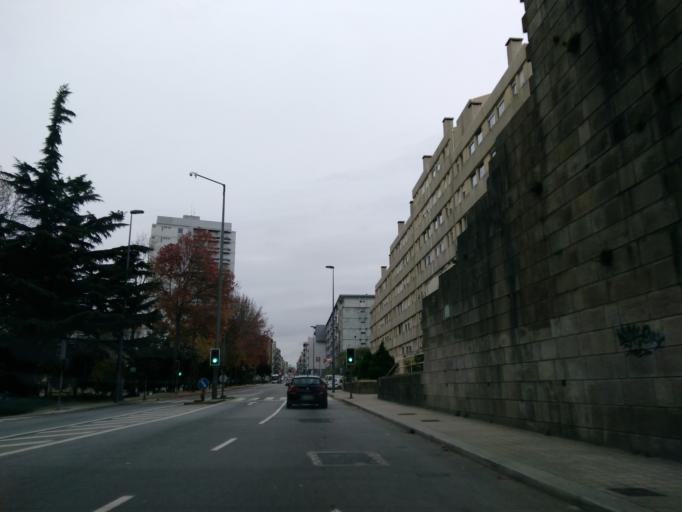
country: PT
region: Porto
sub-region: Porto
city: Porto
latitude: 41.1521
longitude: -8.5970
